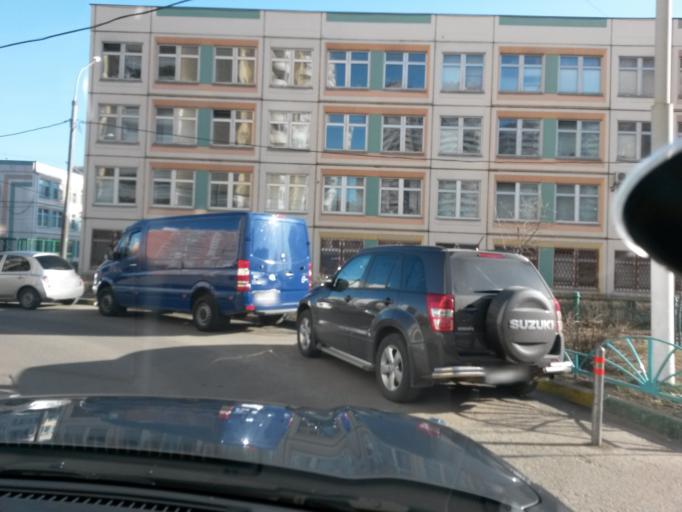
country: RU
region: Moscow
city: Annino
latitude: 55.5656
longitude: 37.5818
